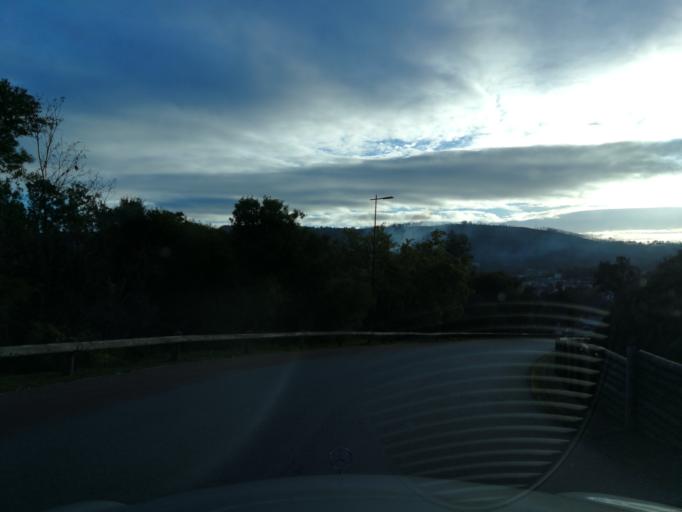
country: PT
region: Braga
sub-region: Braga
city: Braga
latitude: 41.5387
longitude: -8.4144
